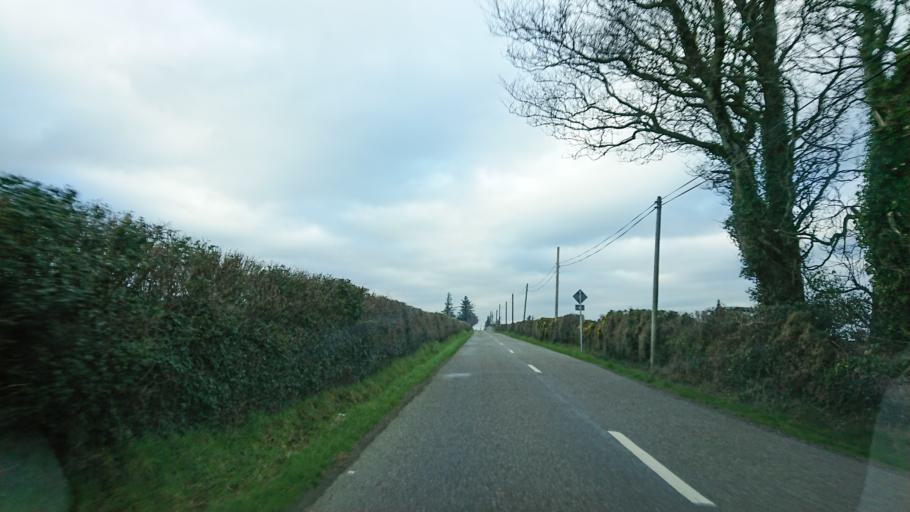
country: IE
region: Munster
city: Carrick-on-Suir
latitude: 52.3115
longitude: -7.5207
